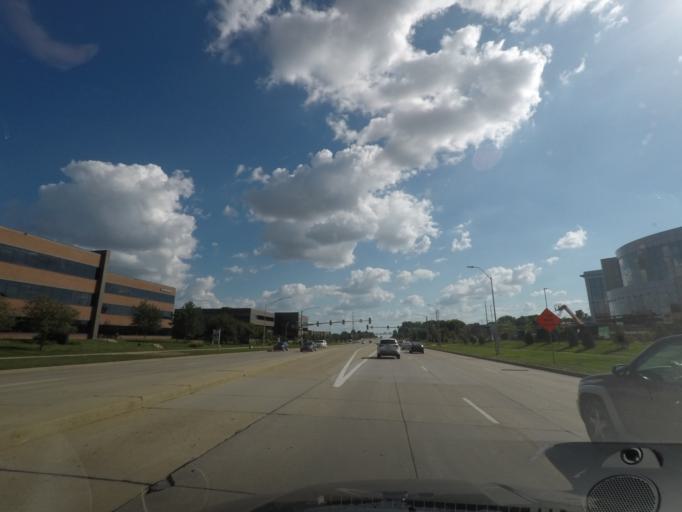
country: US
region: Iowa
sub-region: Dallas County
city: Waukee
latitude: 41.5858
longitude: -93.8092
